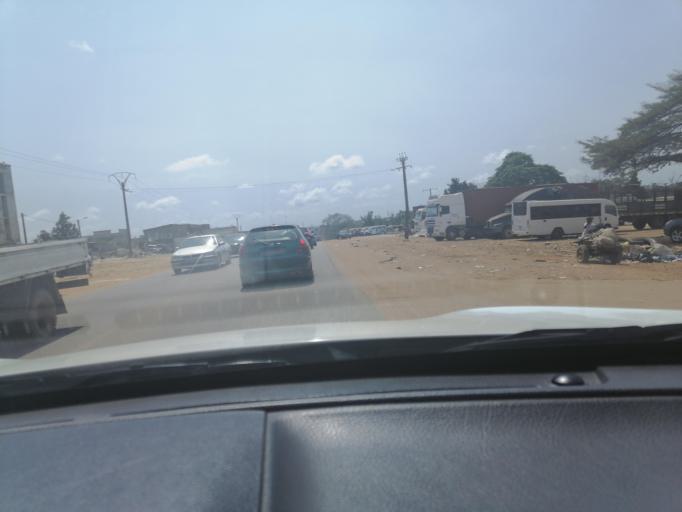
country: CI
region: Lagunes
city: Abidjan
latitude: 5.3485
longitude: -4.1052
